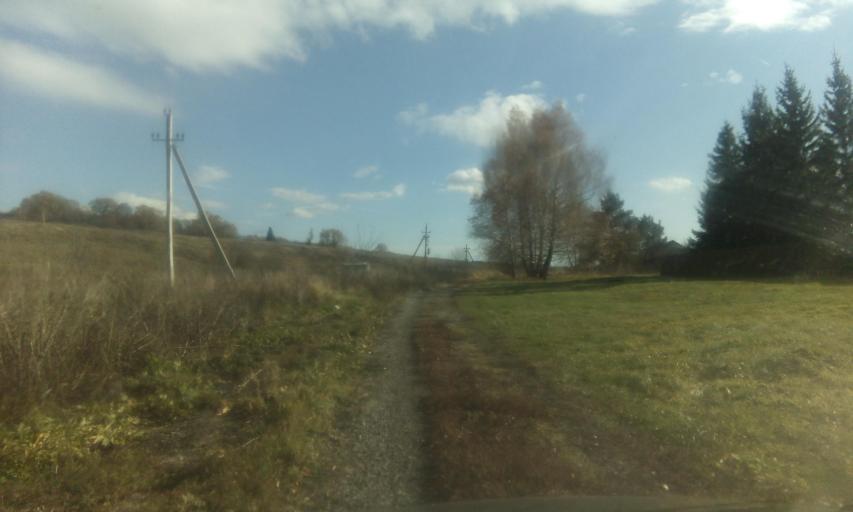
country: RU
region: Tula
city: Dubovka
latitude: 53.9160
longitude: 38.0667
